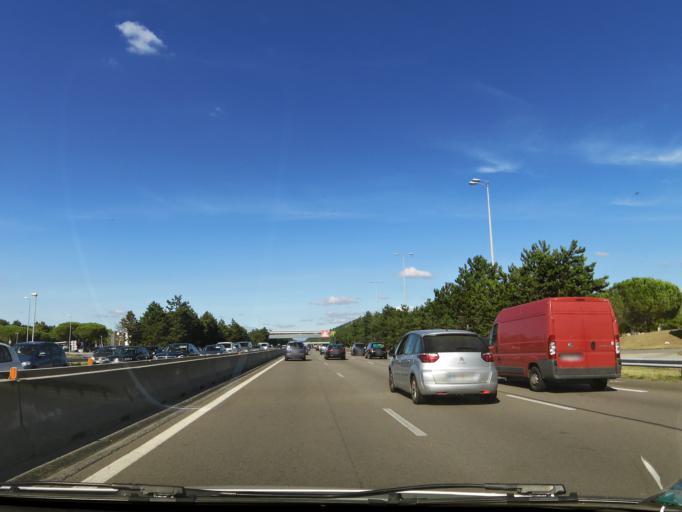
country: FR
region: Rhone-Alpes
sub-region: Departement de la Drome
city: Allan
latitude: 44.5140
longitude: 4.7800
